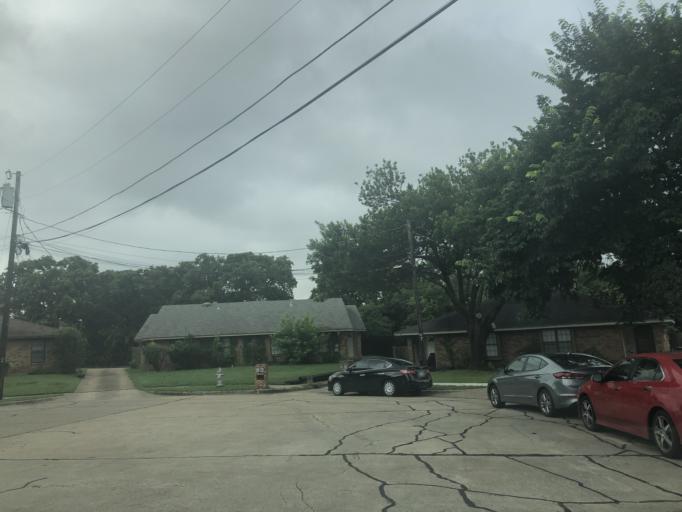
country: US
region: Texas
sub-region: Dallas County
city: Irving
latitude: 32.8104
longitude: -96.9916
